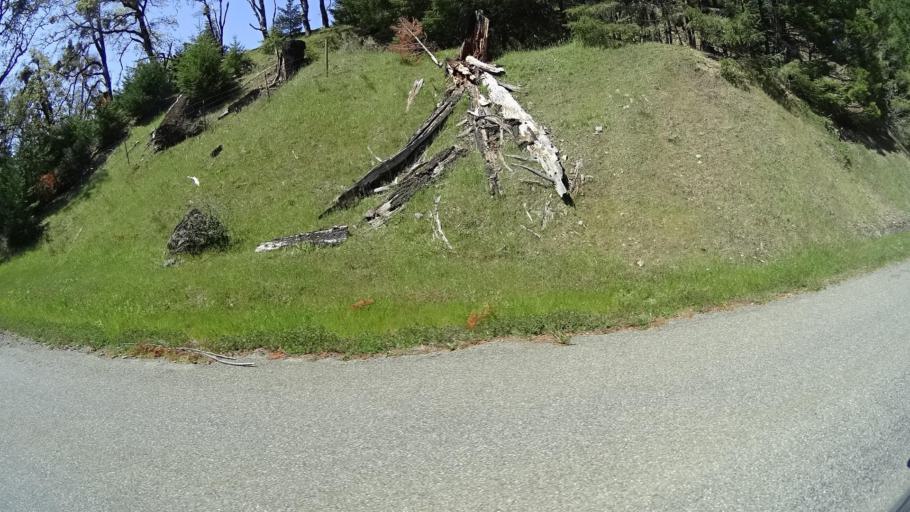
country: US
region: California
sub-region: Humboldt County
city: Redway
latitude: 40.1018
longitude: -123.6842
